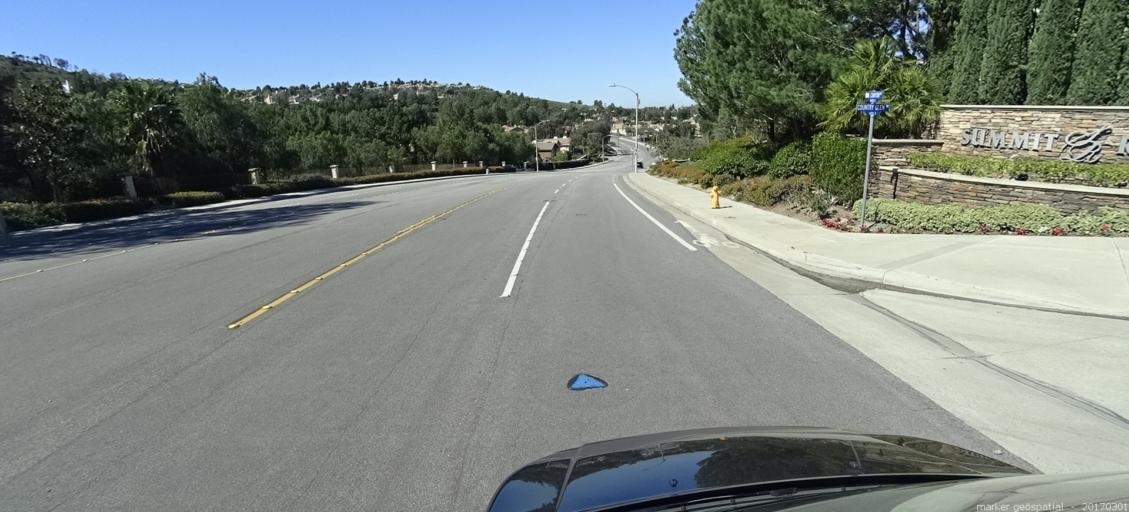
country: US
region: California
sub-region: Orange County
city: Yorba Linda
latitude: 33.8561
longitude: -117.7279
